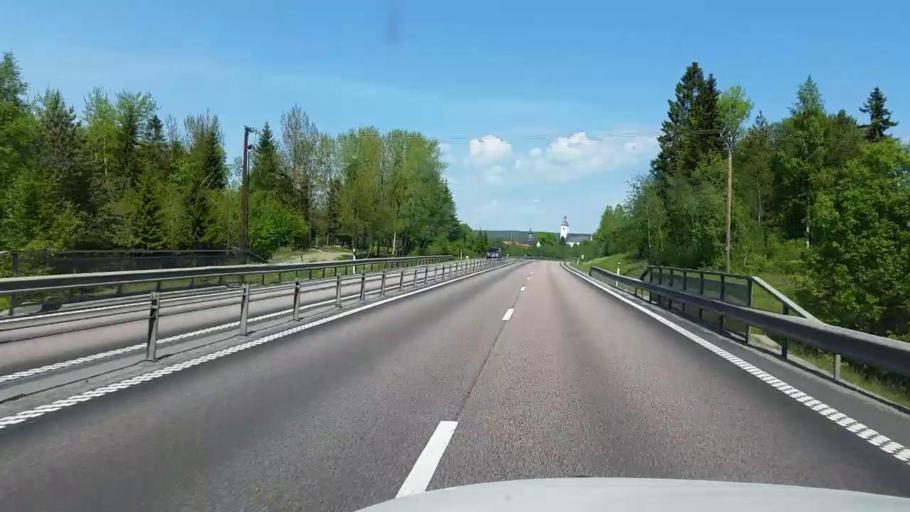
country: SE
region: Gaevleborg
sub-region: Hudiksvalls Kommun
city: Hudiksvall
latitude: 61.7470
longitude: 17.0786
